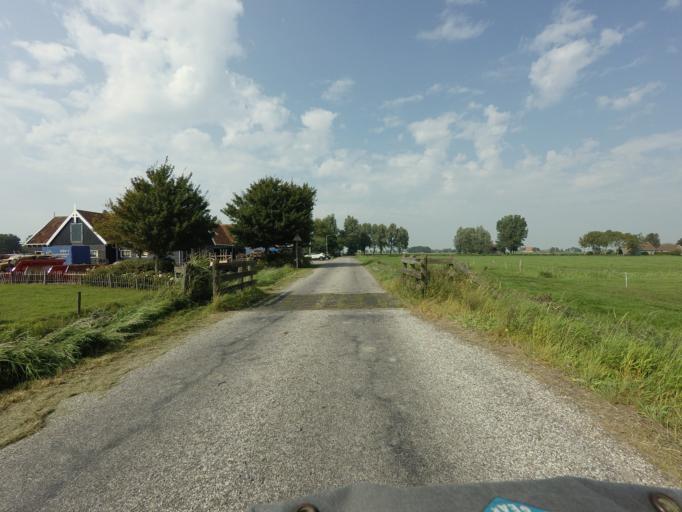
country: NL
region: Friesland
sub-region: Sudwest Fryslan
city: Bolsward
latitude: 53.0189
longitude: 5.5220
